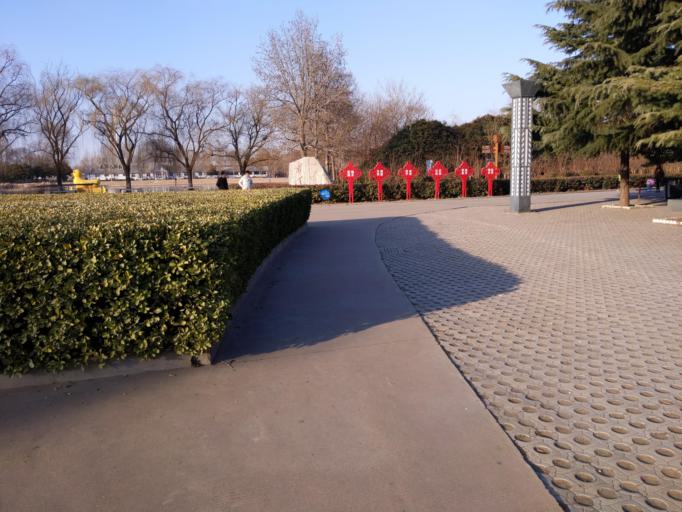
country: CN
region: Henan Sheng
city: Puyang
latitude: 35.7759
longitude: 114.9472
